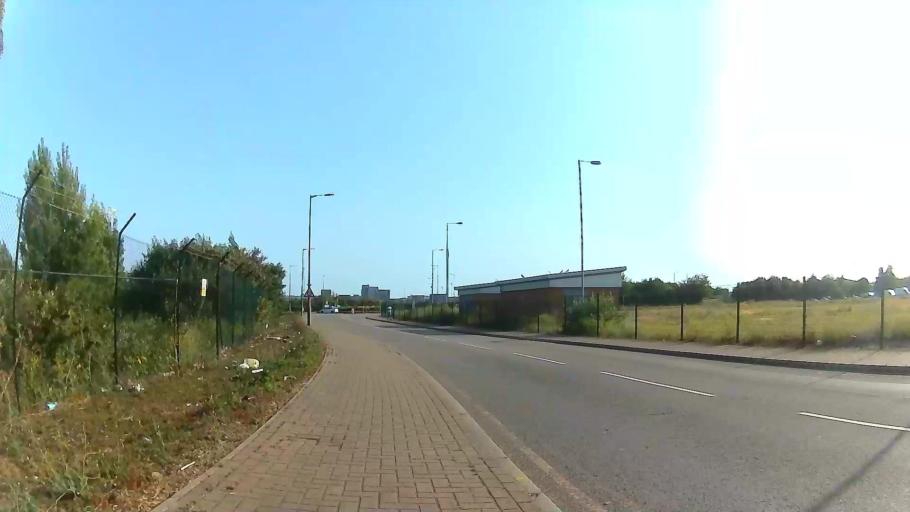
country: GB
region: England
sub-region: Greater London
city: Barking
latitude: 51.5153
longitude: 0.0825
